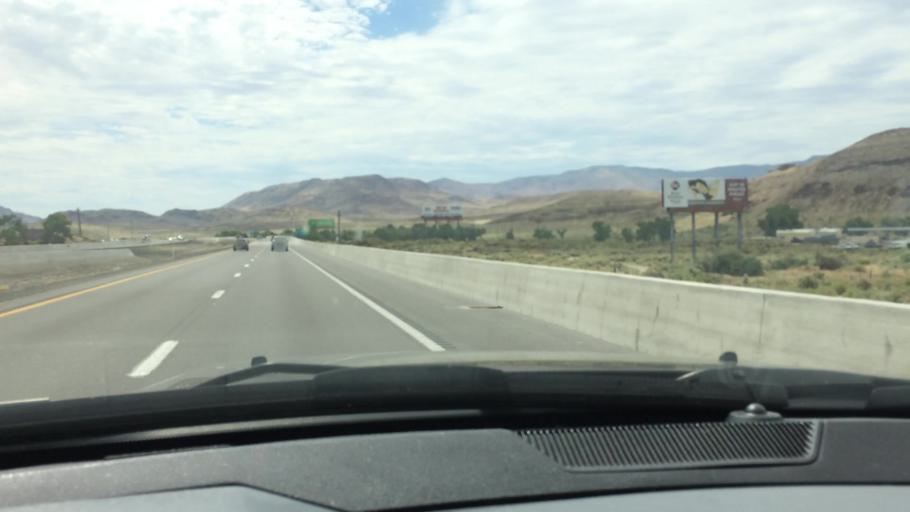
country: US
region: Nevada
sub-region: Lyon County
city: Fernley
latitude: 39.6174
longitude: -119.3015
